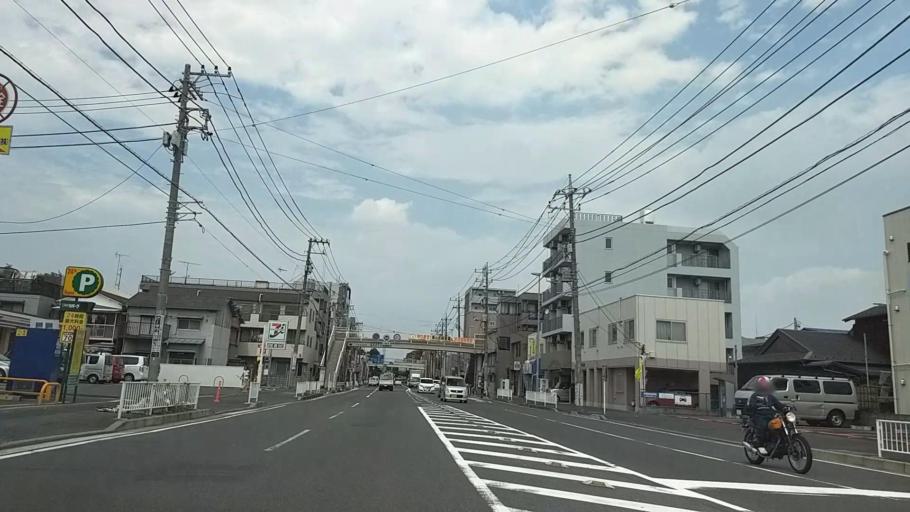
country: JP
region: Kanagawa
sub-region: Kawasaki-shi
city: Kawasaki
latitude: 35.5194
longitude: 139.6726
